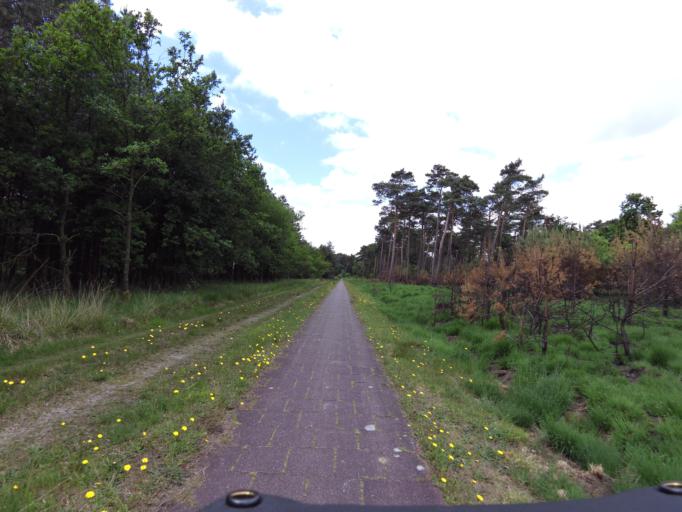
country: NL
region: North Brabant
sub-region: Gemeente Baarle-Nassau
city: Baarle-Nassau
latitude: 51.5007
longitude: 4.9205
